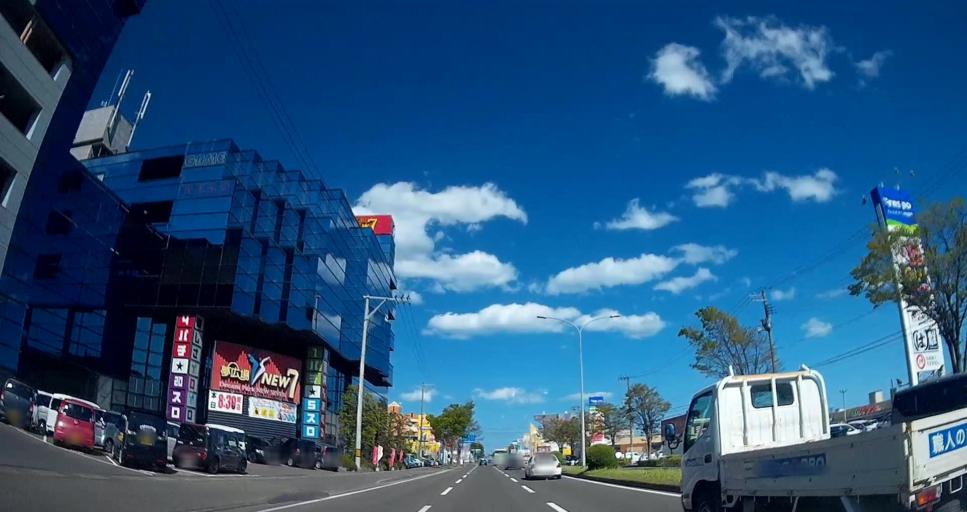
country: JP
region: Miyagi
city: Sendai-shi
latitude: 38.2507
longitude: 140.9436
